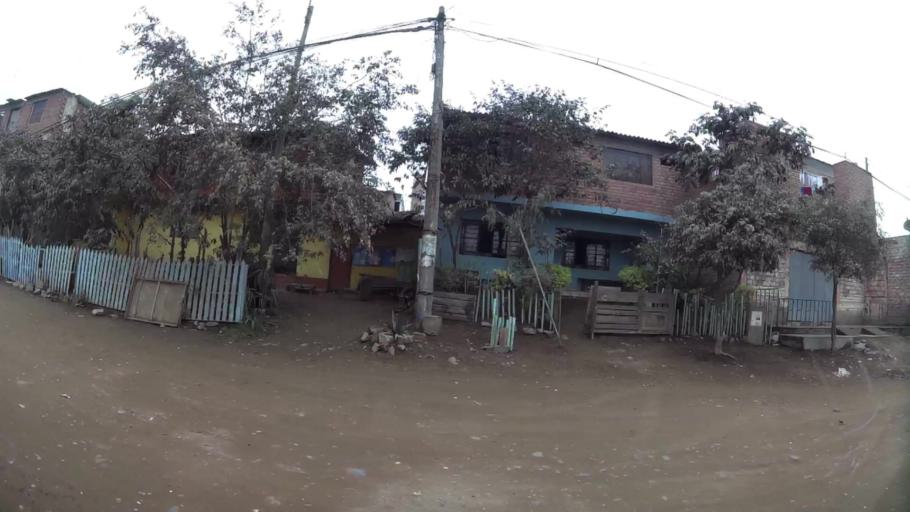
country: PE
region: Lima
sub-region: Lima
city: Surco
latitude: -12.2052
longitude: -76.9252
